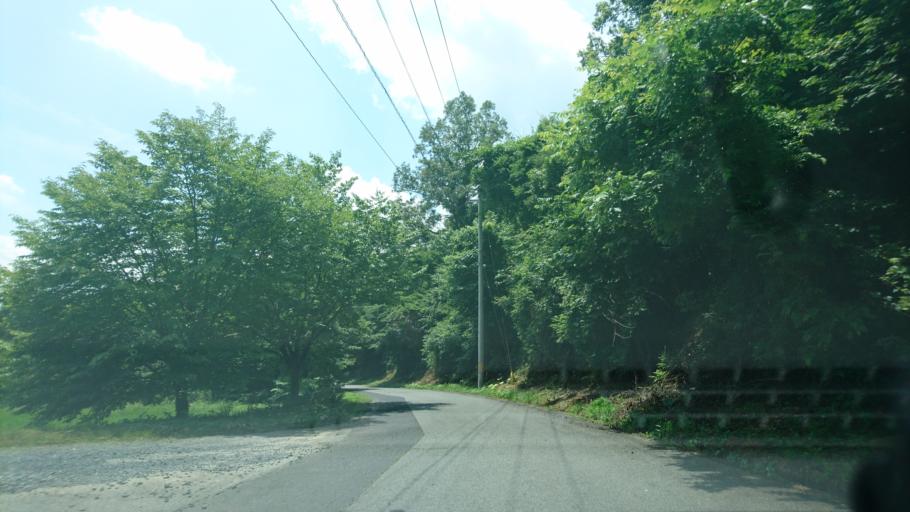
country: JP
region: Iwate
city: Ichinoseki
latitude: 38.9161
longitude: 141.2218
